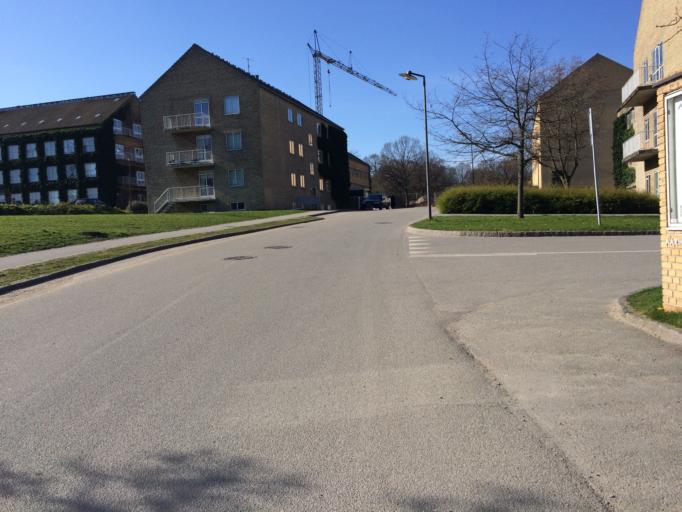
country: DK
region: Central Jutland
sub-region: Arhus Kommune
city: Arhus
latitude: 56.1657
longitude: 10.2057
